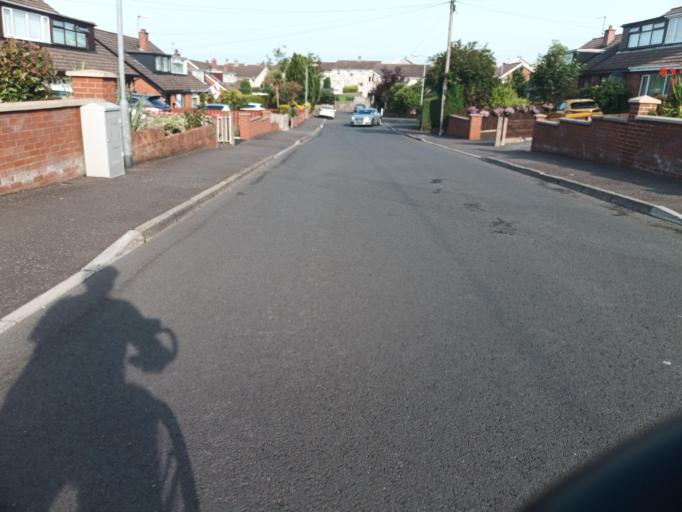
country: GB
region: Northern Ireland
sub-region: Ards District
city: Comber
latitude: 54.5551
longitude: -5.7330
